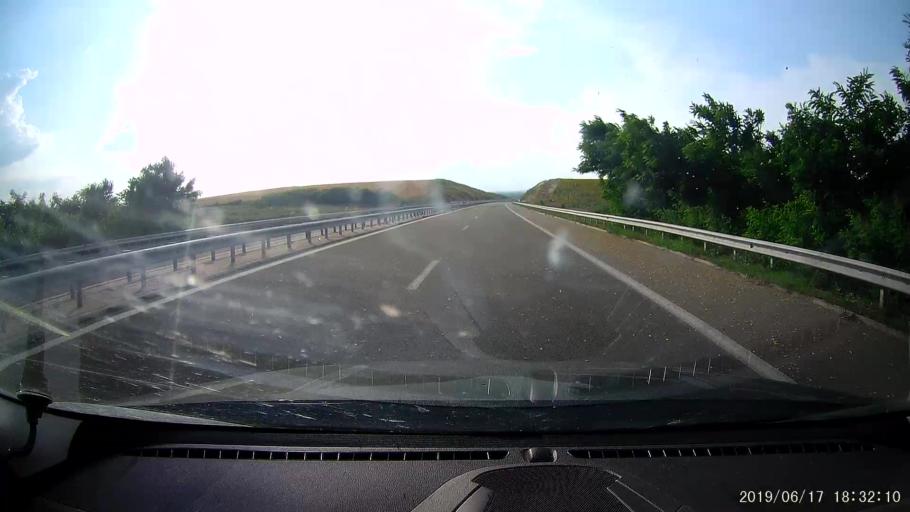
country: BG
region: Khaskovo
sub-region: Obshtina Dimitrovgrad
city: Dimitrovgrad
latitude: 42.0557
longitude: 25.4855
